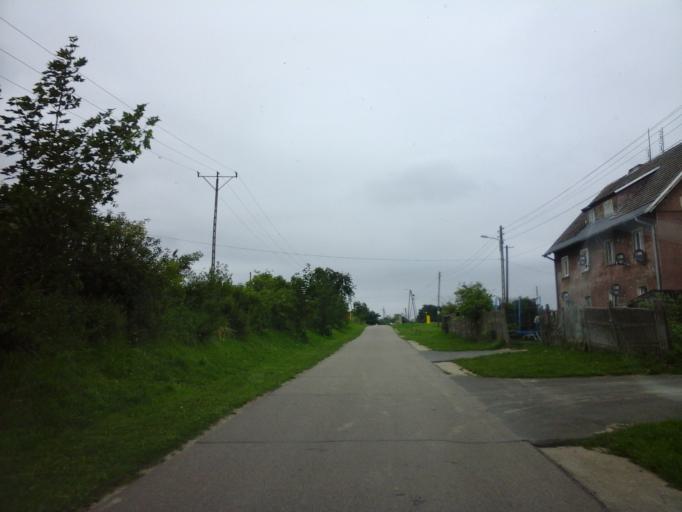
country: PL
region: West Pomeranian Voivodeship
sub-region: Powiat choszczenski
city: Pelczyce
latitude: 53.1032
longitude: 15.3319
